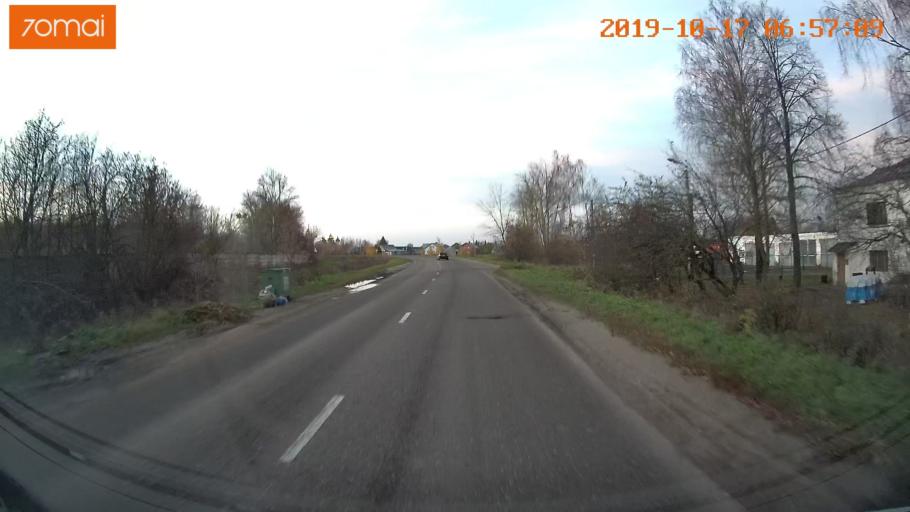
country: RU
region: Vladimir
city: Suzdal'
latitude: 56.4391
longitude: 40.4415
